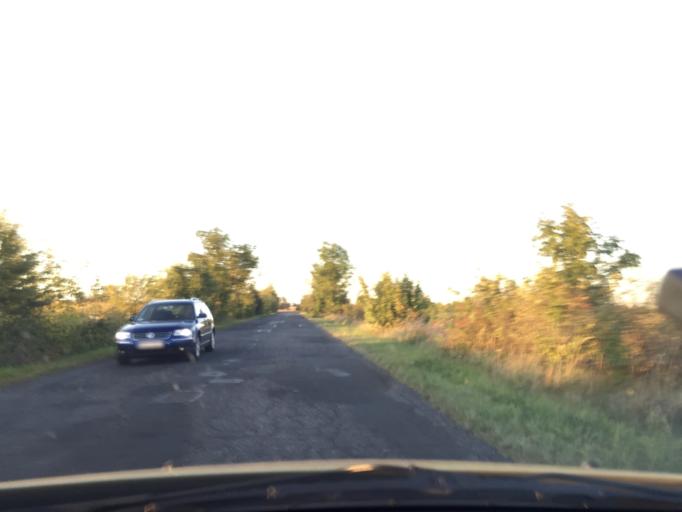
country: PL
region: Greater Poland Voivodeship
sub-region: Powiat pleszewski
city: Dobrzyca
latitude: 51.8315
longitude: 17.6201
